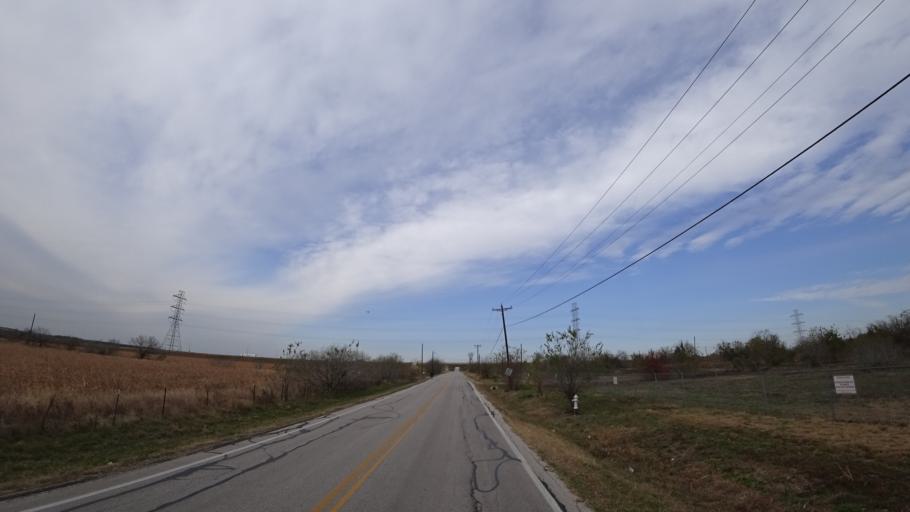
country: US
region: Texas
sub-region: Travis County
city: Garfield
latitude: 30.1472
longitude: -97.6559
